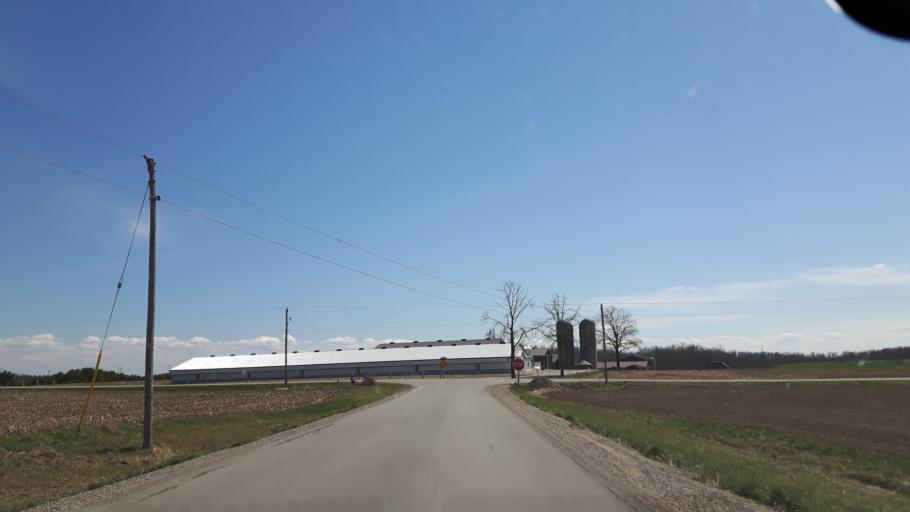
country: CA
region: Ontario
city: Bluewater
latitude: 43.5782
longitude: -81.6438
